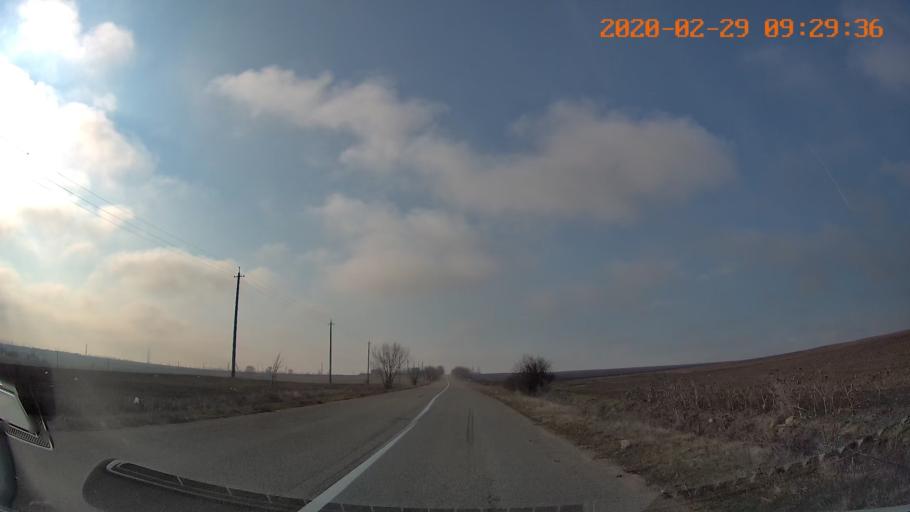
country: UA
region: Odessa
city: Lymanske
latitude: 46.6766
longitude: 29.9204
